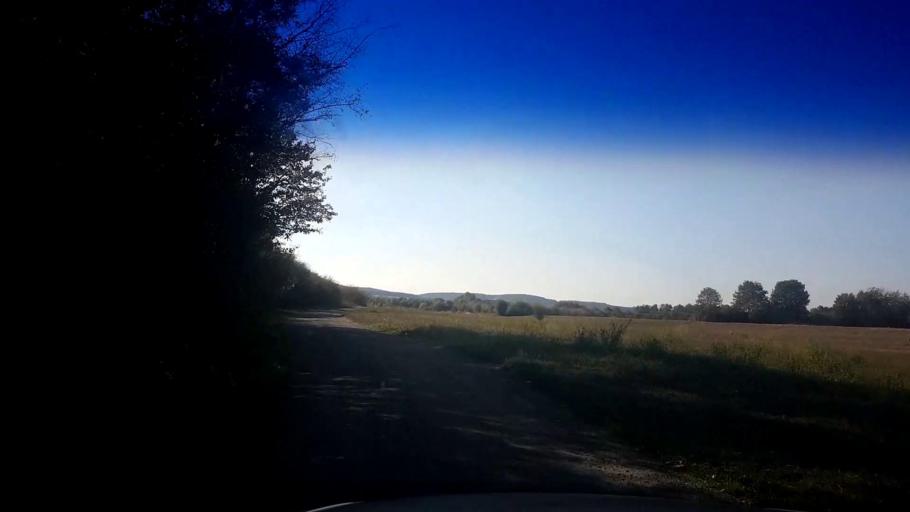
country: DE
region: Bavaria
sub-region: Upper Franconia
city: Viereth-Trunstadt
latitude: 49.9281
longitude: 10.7849
